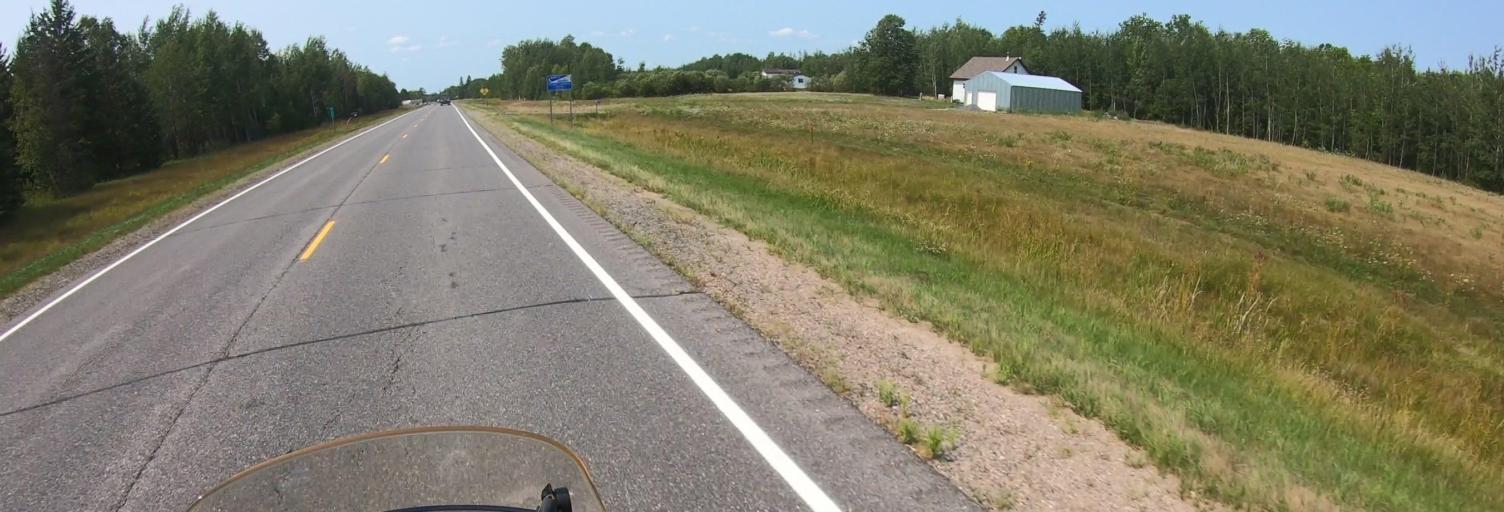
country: US
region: Minnesota
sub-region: Koochiching County
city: International Falls
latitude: 48.5126
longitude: -93.7865
